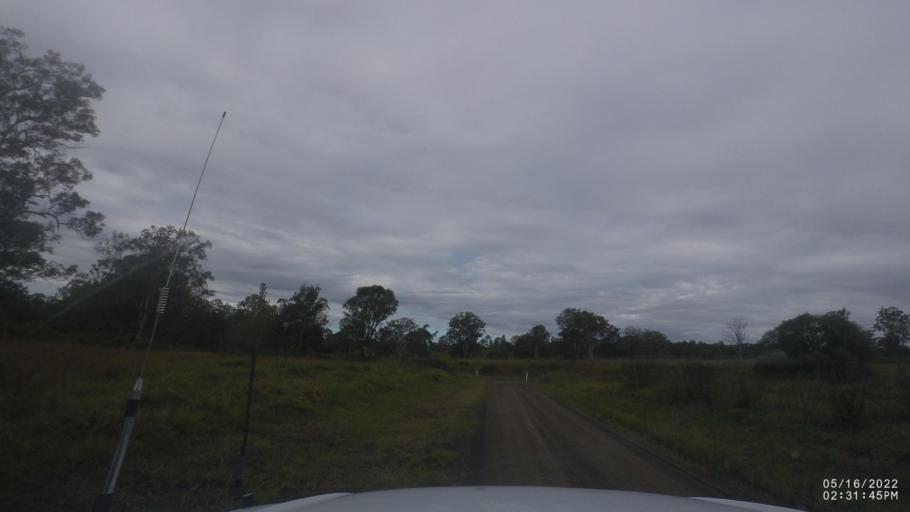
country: AU
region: Queensland
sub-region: Logan
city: Cedar Vale
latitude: -27.8567
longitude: 152.8660
